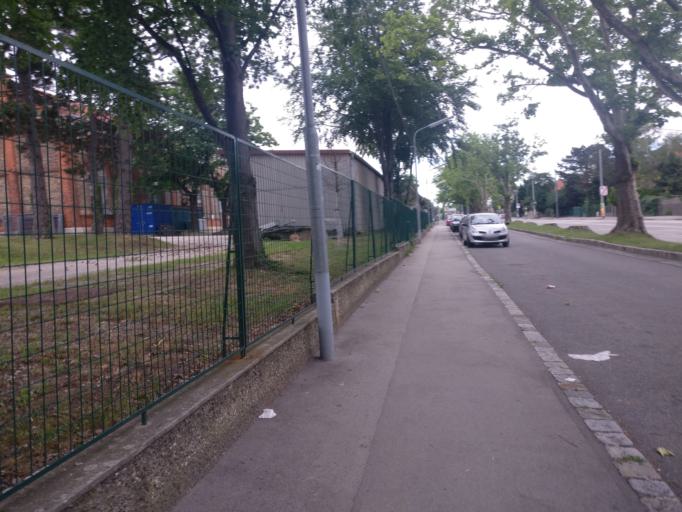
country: AT
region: Vienna
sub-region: Wien Stadt
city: Vienna
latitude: 48.1689
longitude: 16.3522
